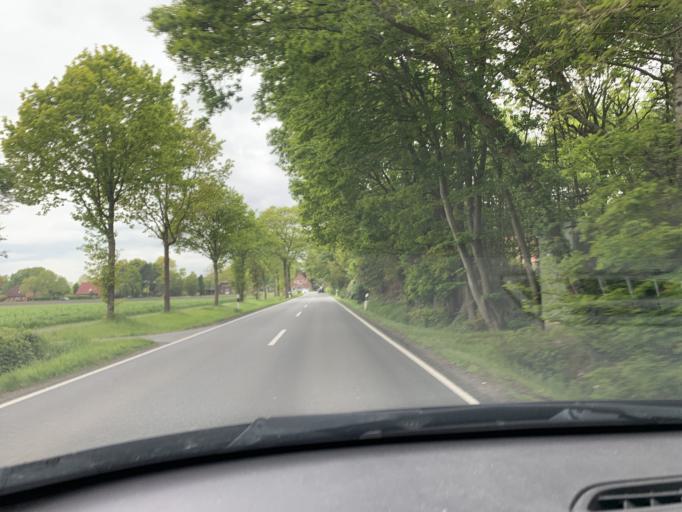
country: DE
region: Lower Saxony
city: Bad Zwischenahn
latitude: 53.2297
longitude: 7.9990
